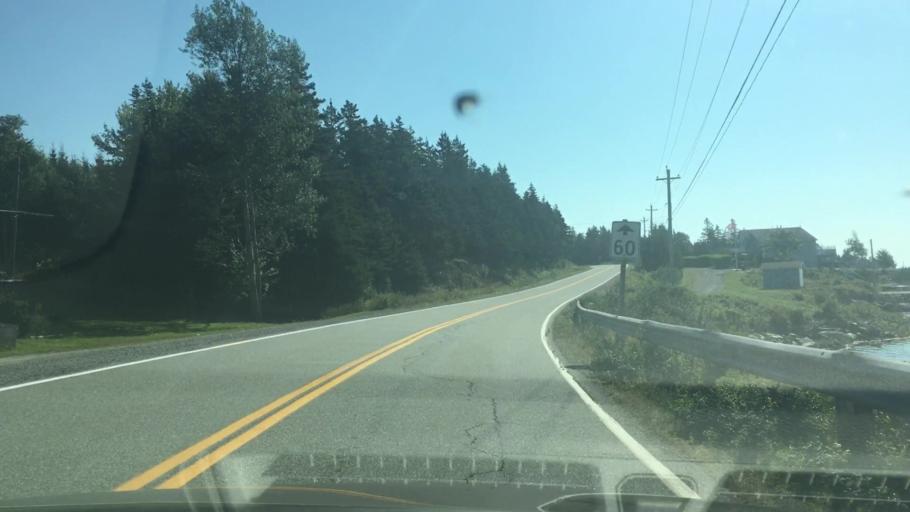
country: CA
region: Nova Scotia
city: Cole Harbour
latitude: 44.8048
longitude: -62.7060
